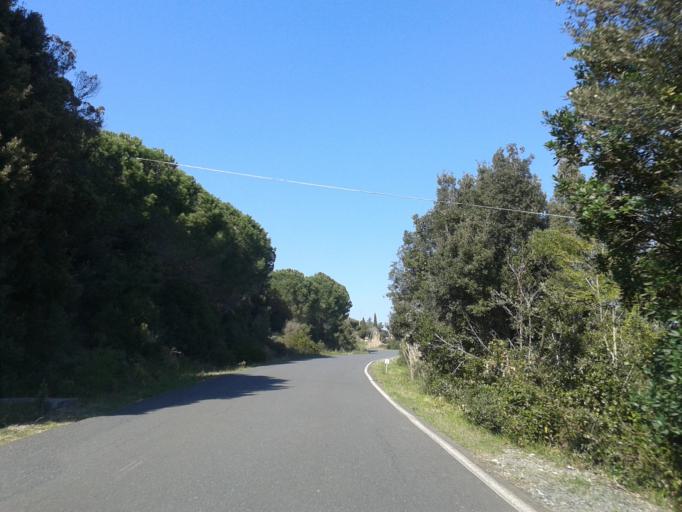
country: IT
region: Tuscany
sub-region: Provincia di Livorno
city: Quercianella
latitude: 43.4572
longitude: 10.4070
